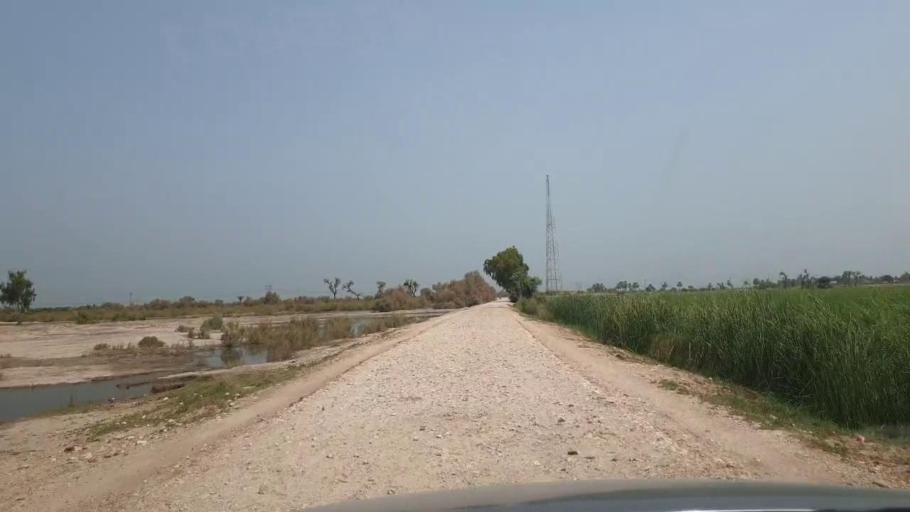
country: PK
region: Sindh
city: Madeji
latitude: 27.8013
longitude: 68.5316
